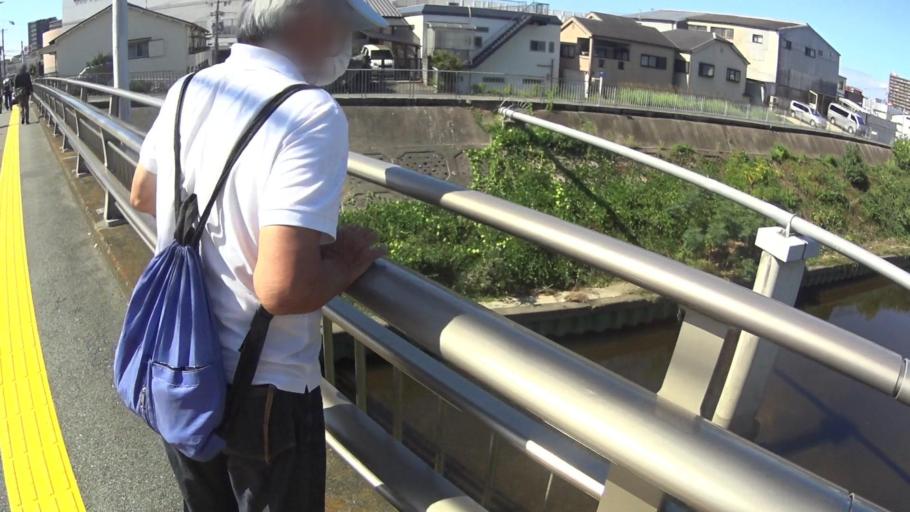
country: JP
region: Osaka
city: Sakai
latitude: 34.5345
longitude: 135.4822
